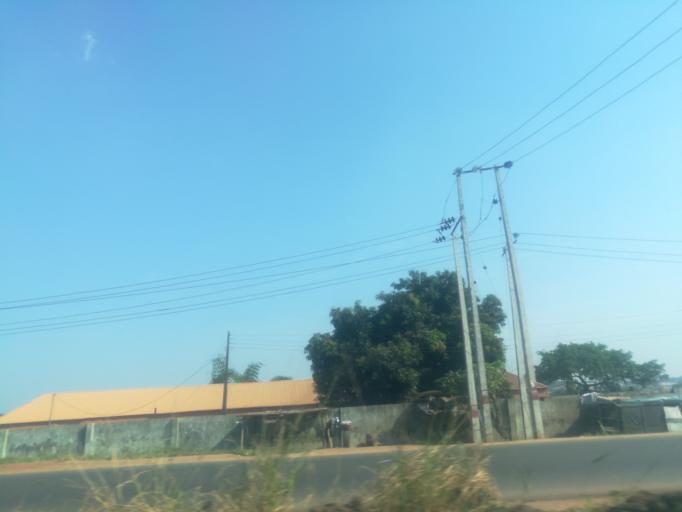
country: NG
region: Ogun
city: Abeokuta
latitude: 7.1431
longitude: 3.3156
